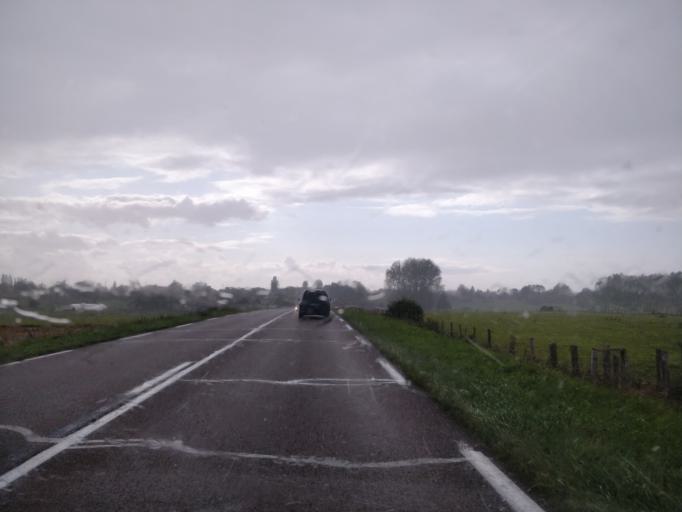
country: FR
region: Champagne-Ardenne
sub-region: Departement de l'Aube
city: Lusigny-sur-Barse
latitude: 48.2399
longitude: 4.3062
